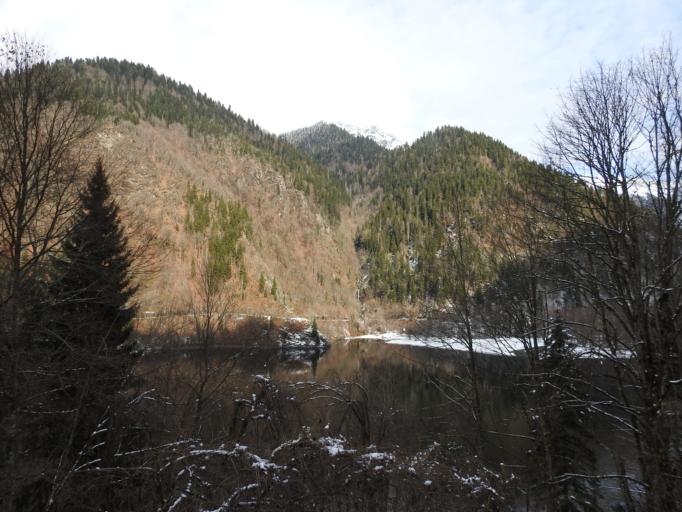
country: GE
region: Abkhazia
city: Gagra
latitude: 43.4784
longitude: 40.5532
